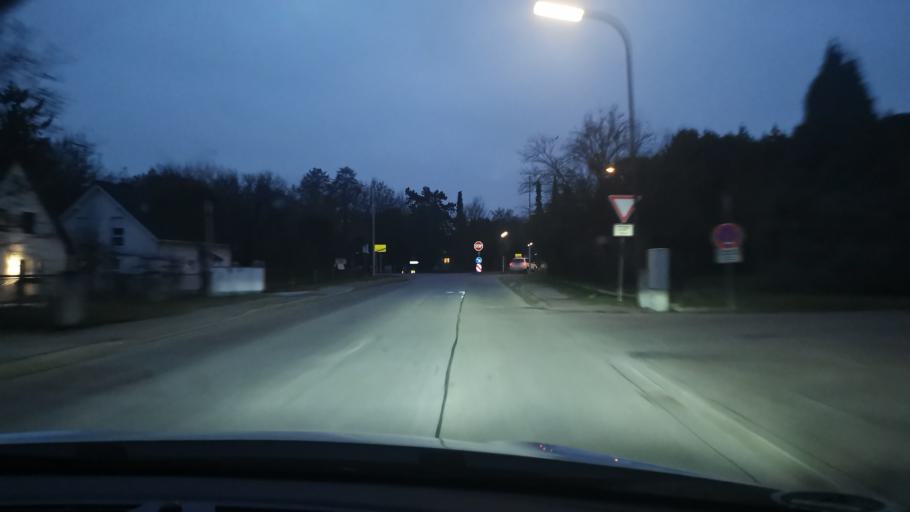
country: DE
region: Bavaria
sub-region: Swabia
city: Pottmes
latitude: 48.5800
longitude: 11.0818
